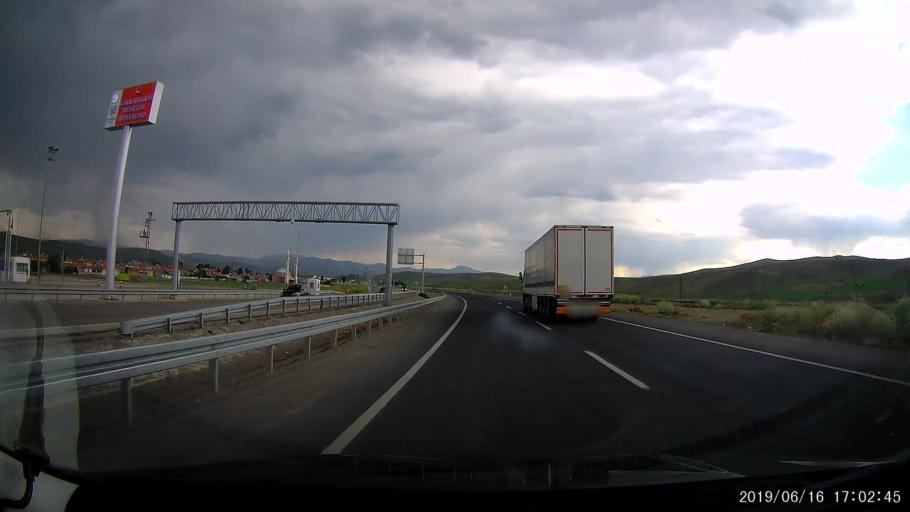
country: TR
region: Erzurum
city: Askale
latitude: 39.9407
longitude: 40.7470
